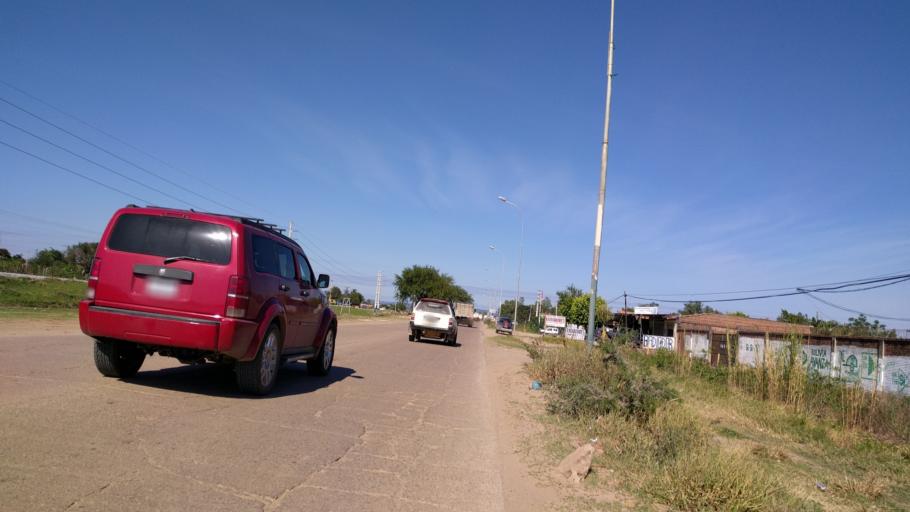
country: BO
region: Santa Cruz
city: Santa Cruz de la Sierra
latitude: -17.8705
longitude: -63.1916
